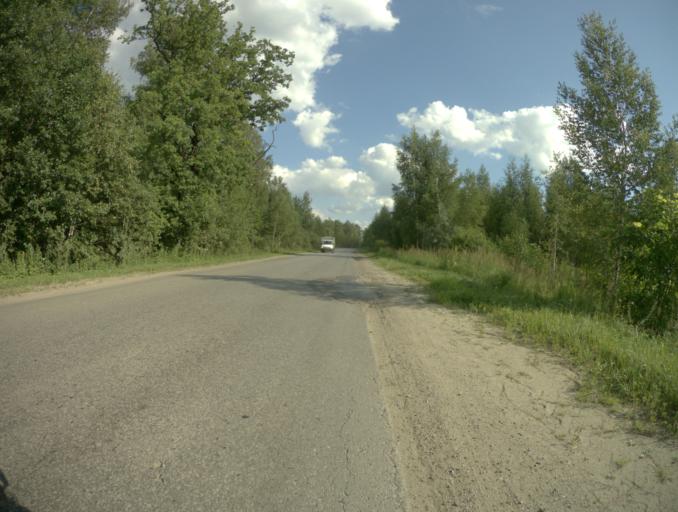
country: RU
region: Vladimir
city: Raduzhnyy
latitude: 56.0661
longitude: 40.3672
